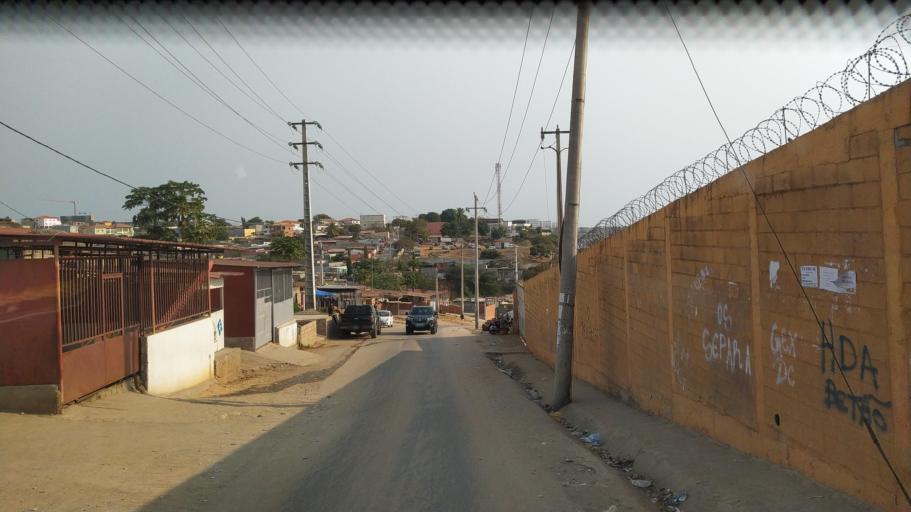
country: AO
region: Luanda
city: Luanda
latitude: -8.8702
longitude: 13.1986
